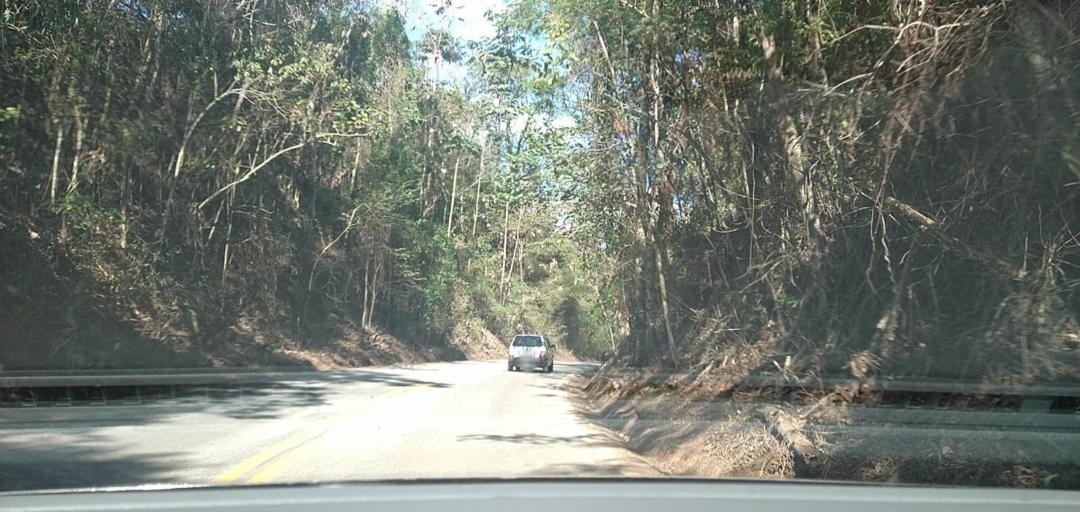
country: BR
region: Minas Gerais
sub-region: Alvinopolis
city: Alvinopolis
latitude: -20.0353
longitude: -43.0376
